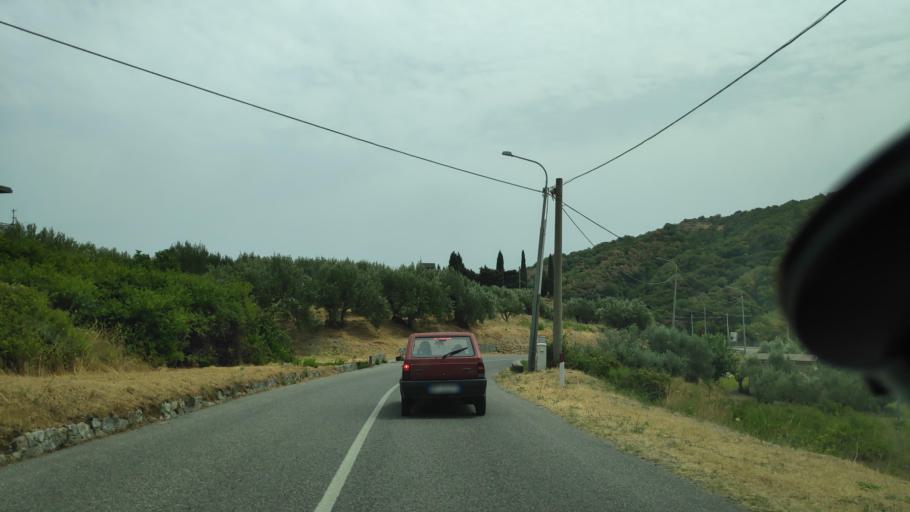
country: IT
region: Calabria
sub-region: Provincia di Catanzaro
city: Davoli
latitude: 38.6561
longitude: 16.4901
